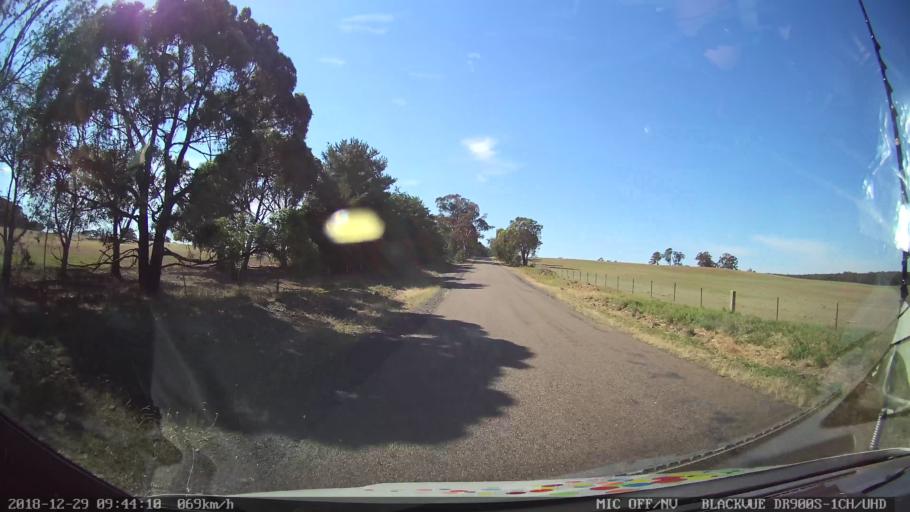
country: AU
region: New South Wales
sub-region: Upper Lachlan Shire
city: Crookwell
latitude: -34.6866
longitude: 149.4251
